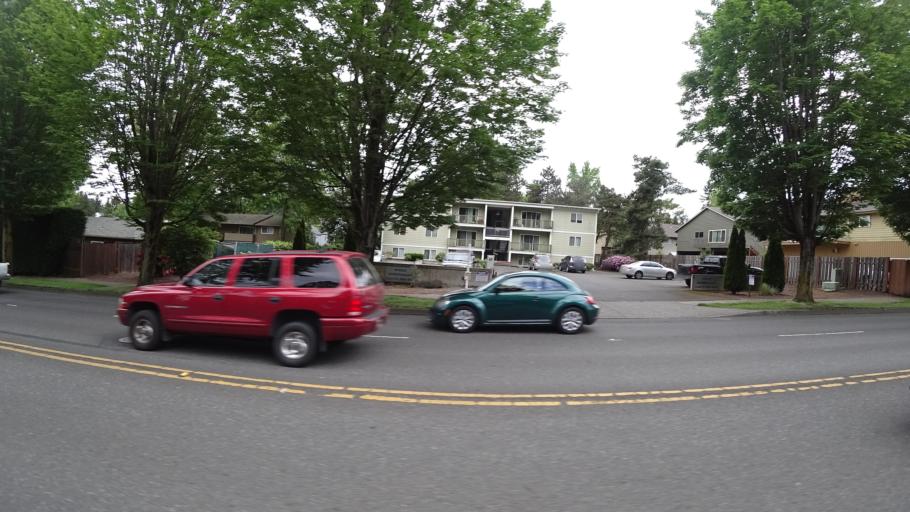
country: US
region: Oregon
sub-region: Washington County
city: Beaverton
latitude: 45.4765
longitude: -122.8139
